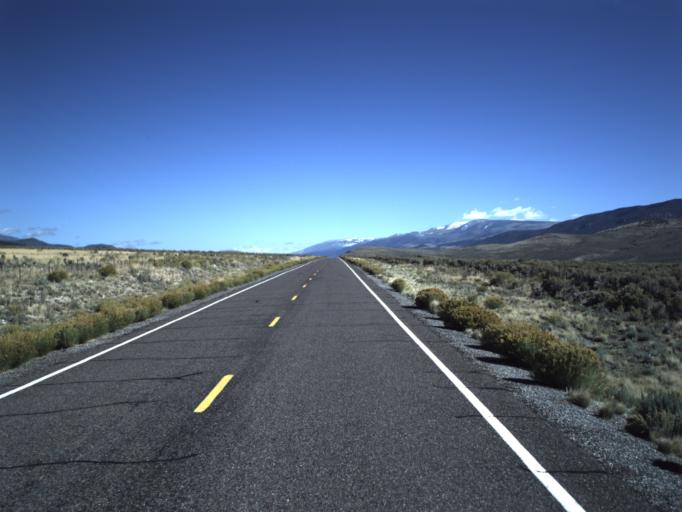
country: US
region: Utah
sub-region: Piute County
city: Junction
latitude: 38.3263
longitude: -111.9606
